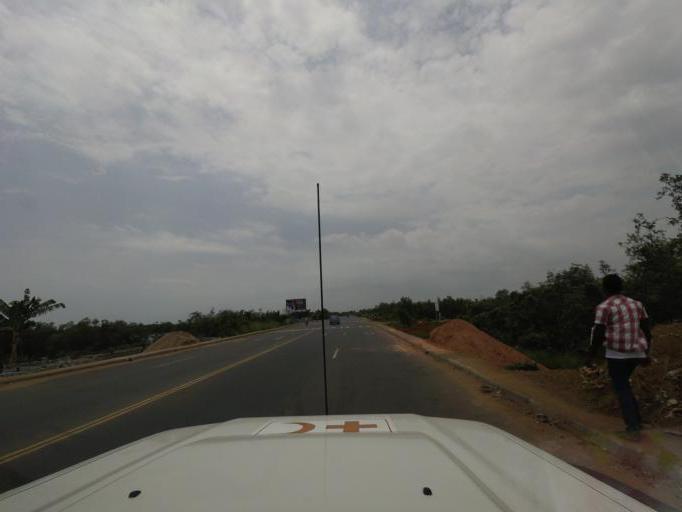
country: LR
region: Montserrado
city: Monrovia
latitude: 6.2799
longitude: -10.7147
